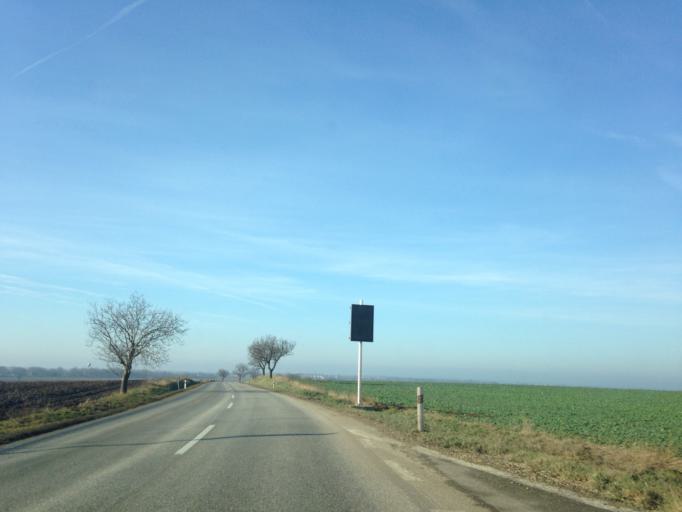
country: SK
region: Nitriansky
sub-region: Okres Nove Zamky
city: Nove Zamky
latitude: 47.9925
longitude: 18.3126
